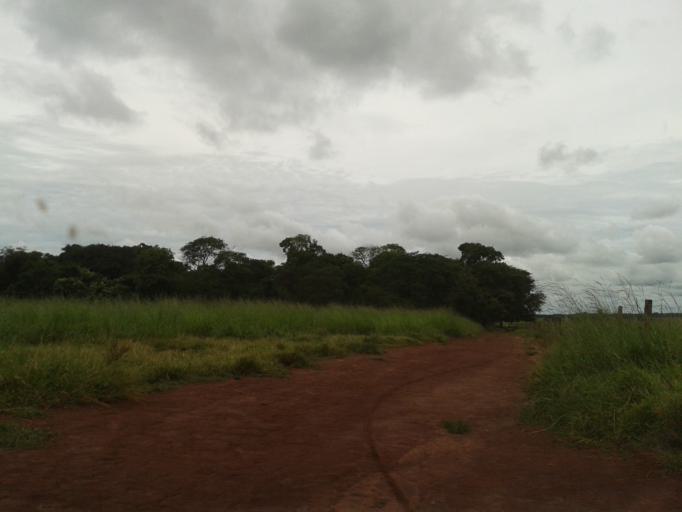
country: BR
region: Minas Gerais
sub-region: Capinopolis
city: Capinopolis
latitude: -18.7858
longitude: -49.7808
